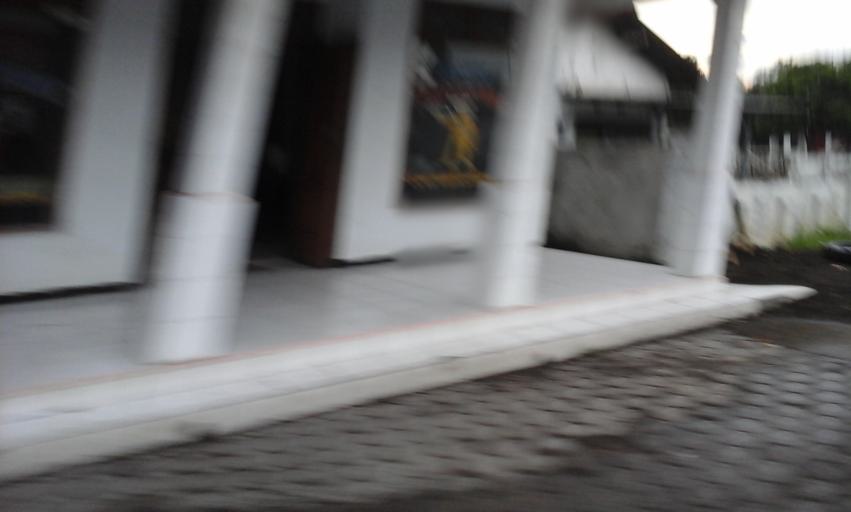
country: ID
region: East Java
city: Muktisari
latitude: -8.2144
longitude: 113.6774
